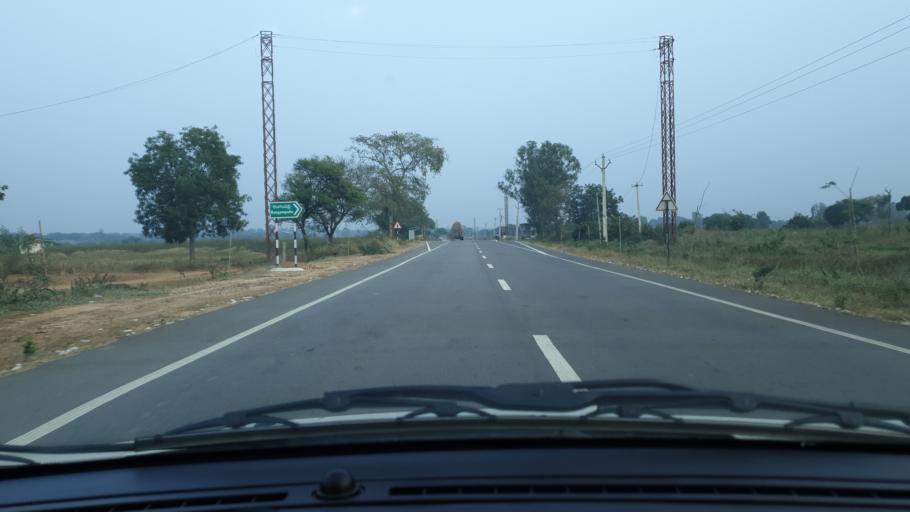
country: IN
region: Telangana
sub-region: Rangareddi
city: Vikarabad
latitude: 17.1653
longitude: 77.8276
